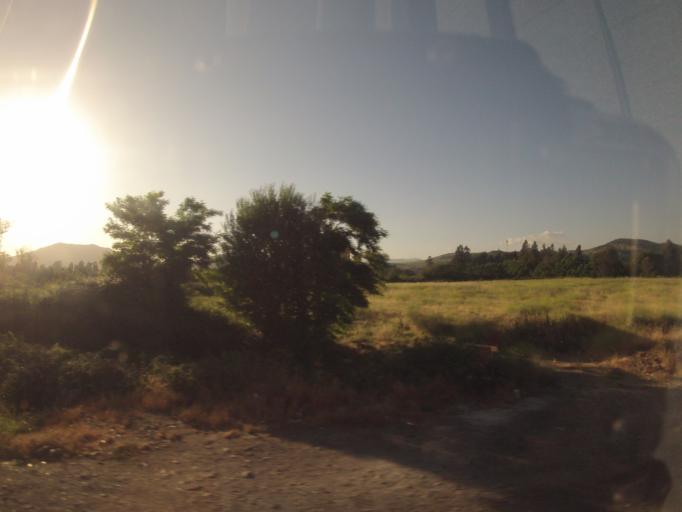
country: CL
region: O'Higgins
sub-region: Provincia de Colchagua
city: Chimbarongo
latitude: -34.6680
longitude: -70.9980
